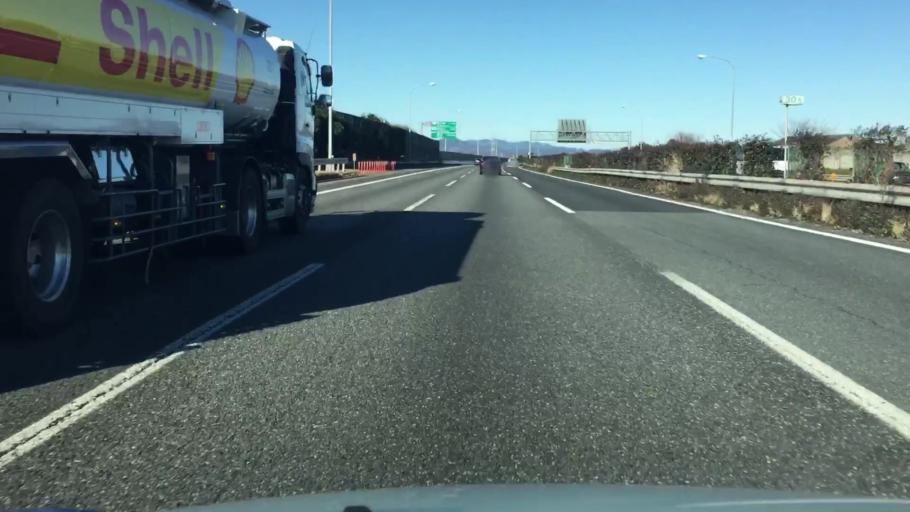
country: JP
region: Saitama
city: Sakado
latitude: 35.9512
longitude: 139.3905
